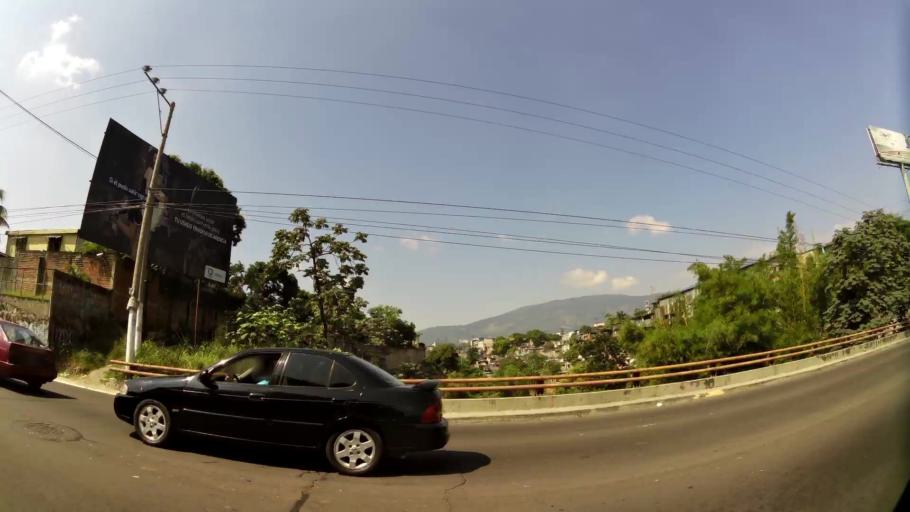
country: SV
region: San Salvador
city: San Salvador
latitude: 13.6927
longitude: -89.2222
